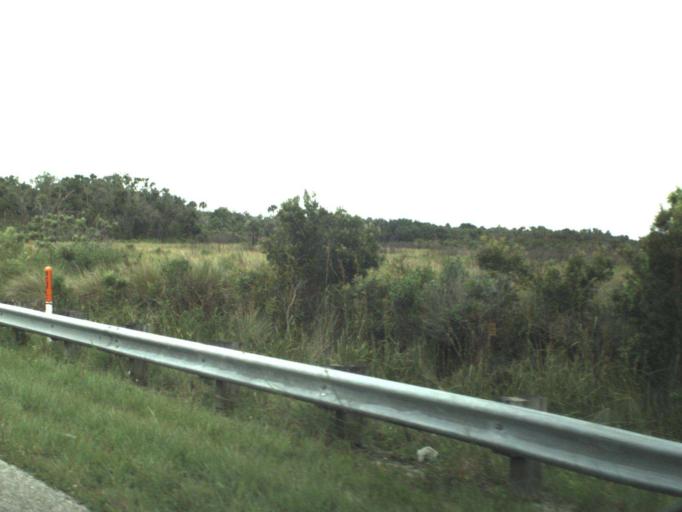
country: US
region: Florida
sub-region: Orange County
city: Christmas
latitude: 28.5437
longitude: -80.9033
